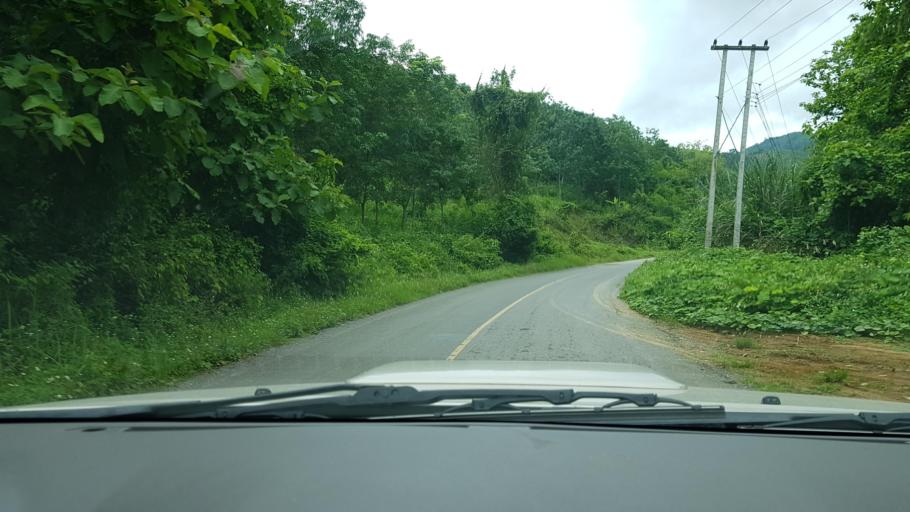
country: LA
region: Loungnamtha
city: Muang Nale
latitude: 20.2455
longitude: 101.5771
